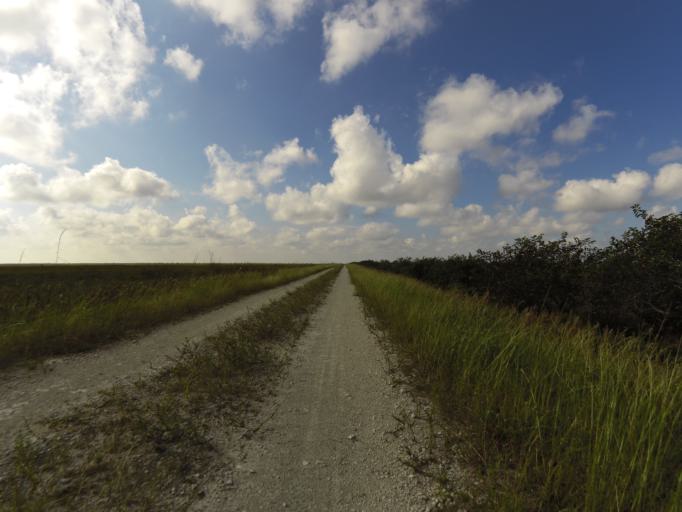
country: US
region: Florida
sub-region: Broward County
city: Weston
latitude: 26.0350
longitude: -80.4922
